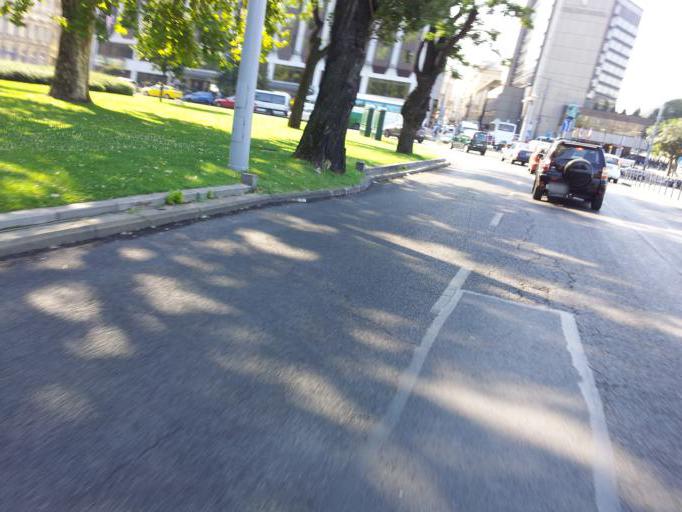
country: HU
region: Budapest
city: Budapest
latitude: 47.4991
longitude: 19.0470
